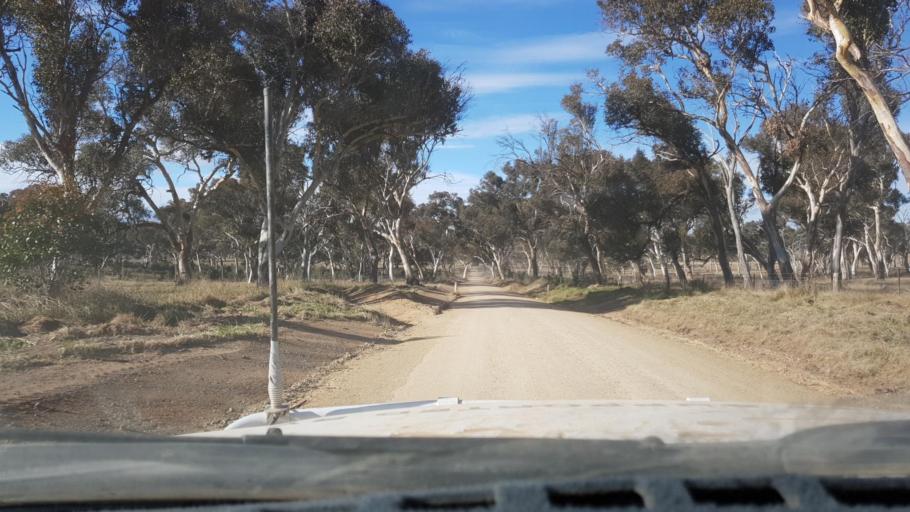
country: AU
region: New South Wales
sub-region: Armidale Dumaresq
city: Enmore
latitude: -30.7192
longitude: 151.5897
